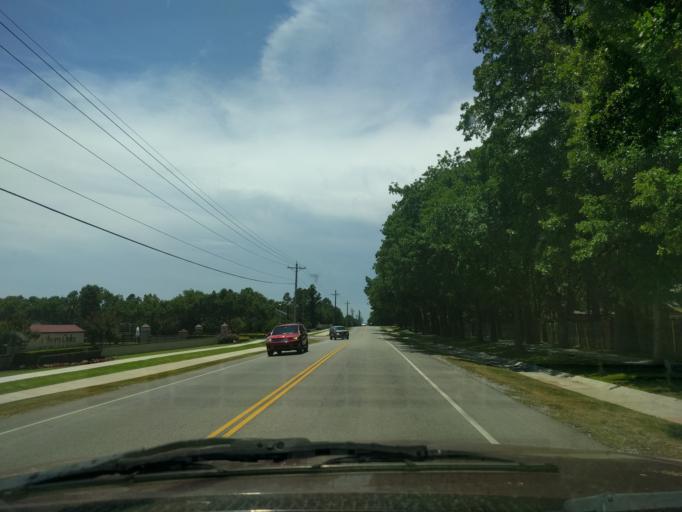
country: US
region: Oklahoma
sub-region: Tulsa County
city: Jenks
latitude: 36.0091
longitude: -95.9222
